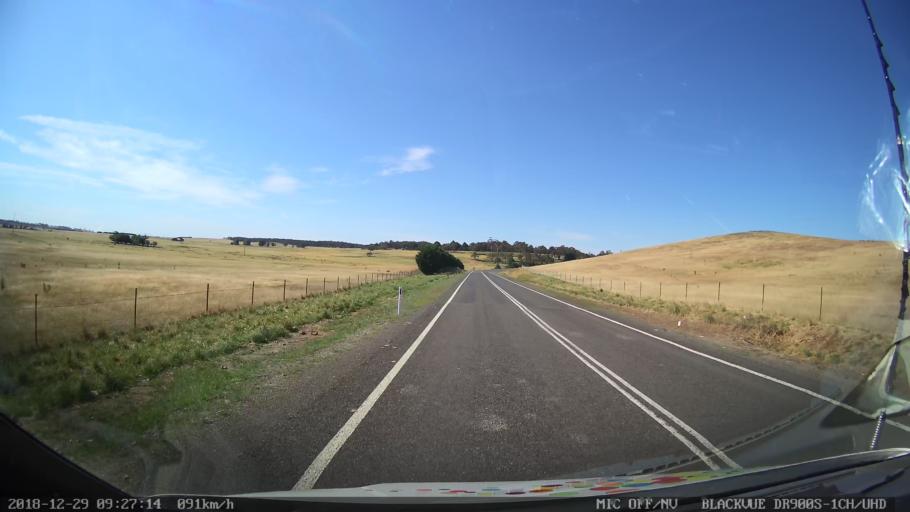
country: AU
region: New South Wales
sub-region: Upper Lachlan Shire
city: Crookwell
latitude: -34.5640
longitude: 149.3856
